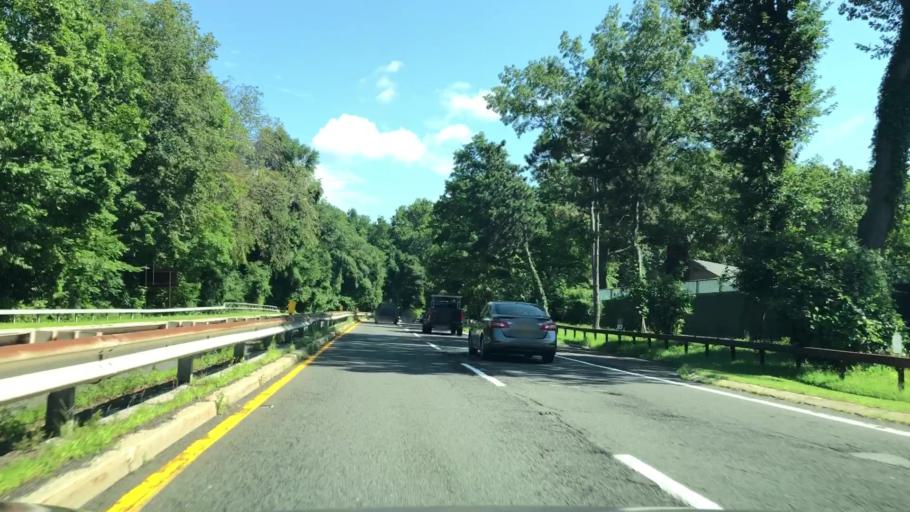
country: US
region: New York
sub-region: Westchester County
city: Hartsdale
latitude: 41.0124
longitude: -73.7935
